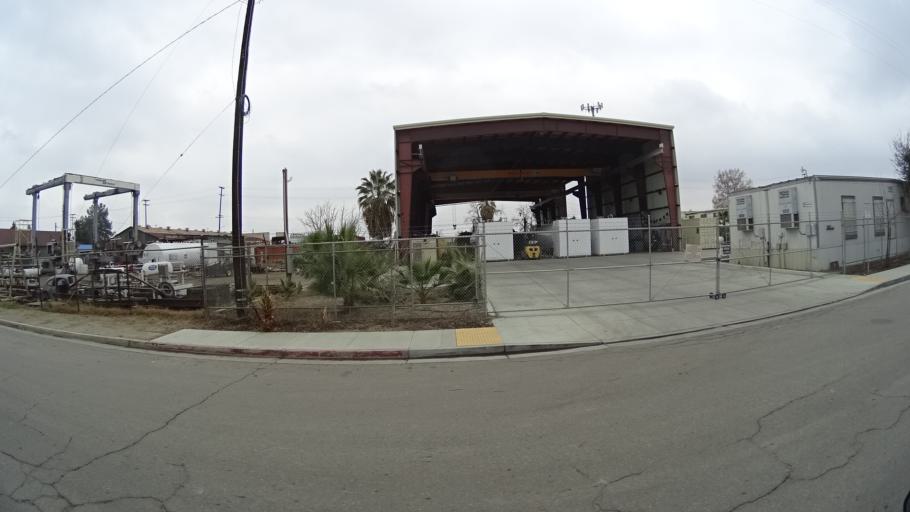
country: US
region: California
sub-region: Kern County
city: Bakersfield
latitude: 35.3886
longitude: -119.0168
